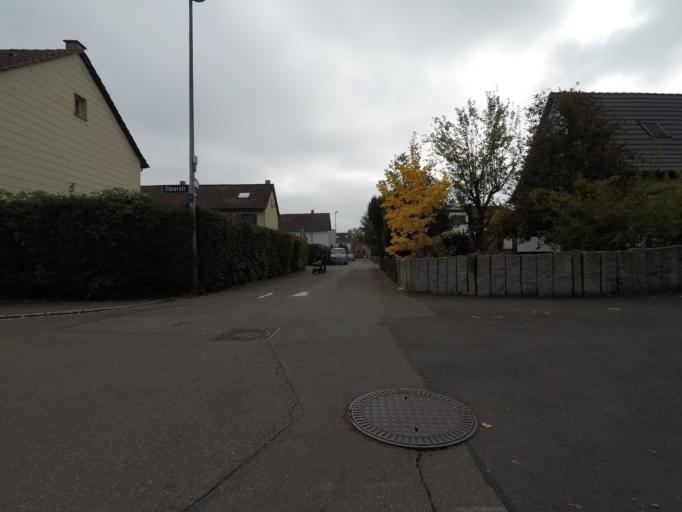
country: DE
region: Baden-Wuerttemberg
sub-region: Tuebingen Region
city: Reutlingen
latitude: 48.5073
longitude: 9.1980
